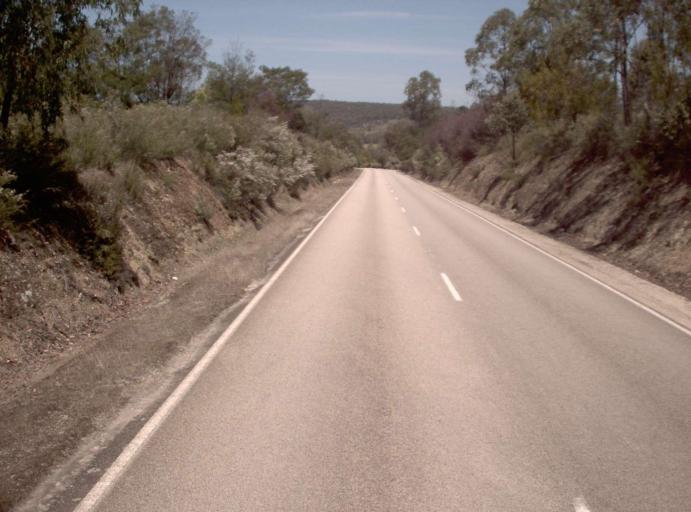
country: AU
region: Victoria
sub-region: East Gippsland
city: Lakes Entrance
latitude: -37.6592
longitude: 147.8783
